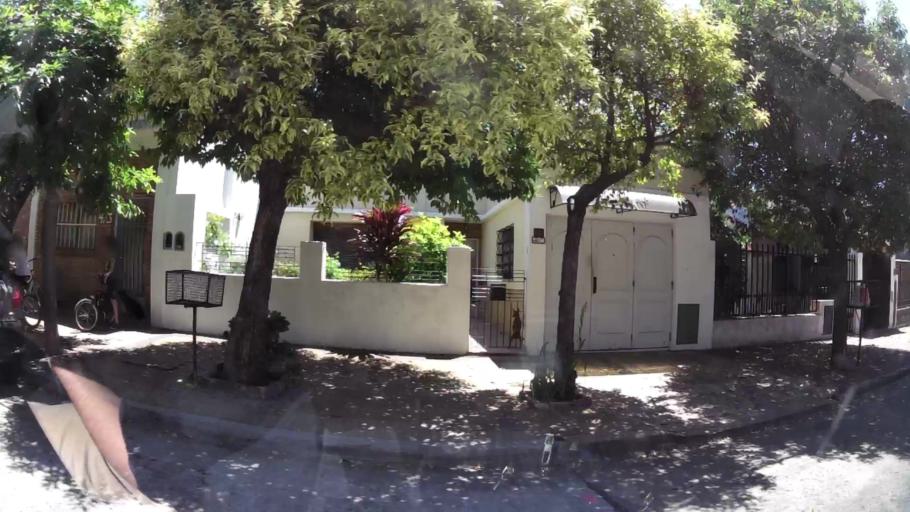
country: AR
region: Buenos Aires
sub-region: Partido de General San Martin
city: General San Martin
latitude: -34.5861
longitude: -58.5432
